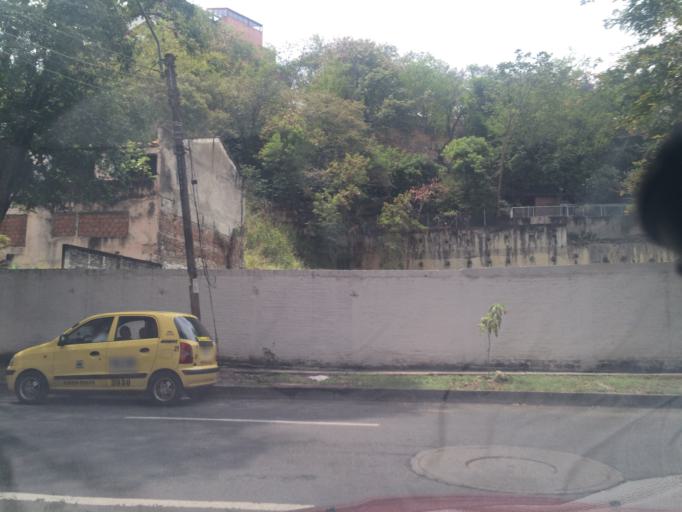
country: CO
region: Valle del Cauca
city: Cali
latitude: 3.4513
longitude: -76.5507
